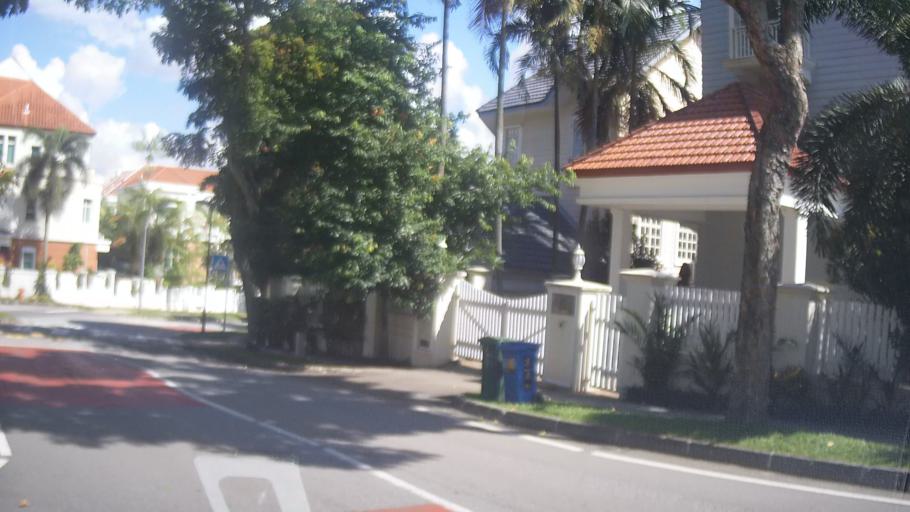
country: MY
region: Johor
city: Johor Bahru
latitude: 1.4275
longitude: 103.7776
